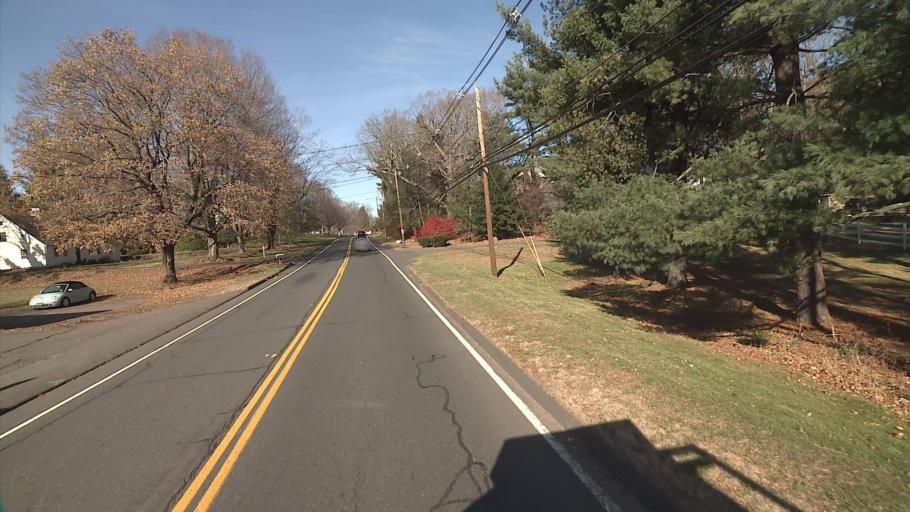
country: US
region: Connecticut
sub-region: Hartford County
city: Glastonbury Center
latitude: 41.6800
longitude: -72.5991
